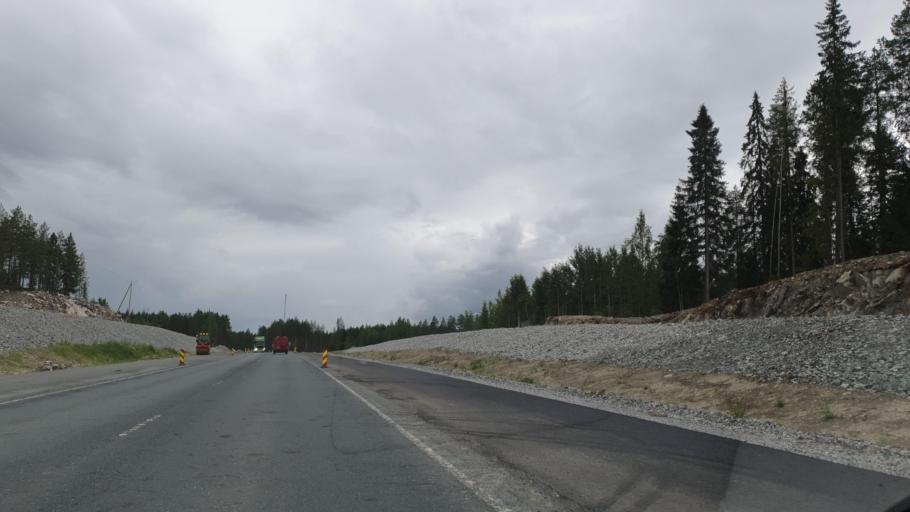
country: FI
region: Northern Savo
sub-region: Ylae-Savo
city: Lapinlahti
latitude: 63.2826
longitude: 27.4555
